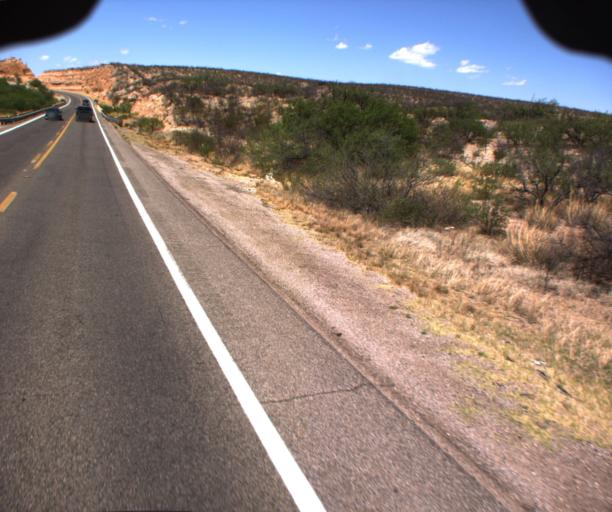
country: US
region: Arizona
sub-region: Cochise County
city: Saint David
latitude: 31.8133
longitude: -110.1653
